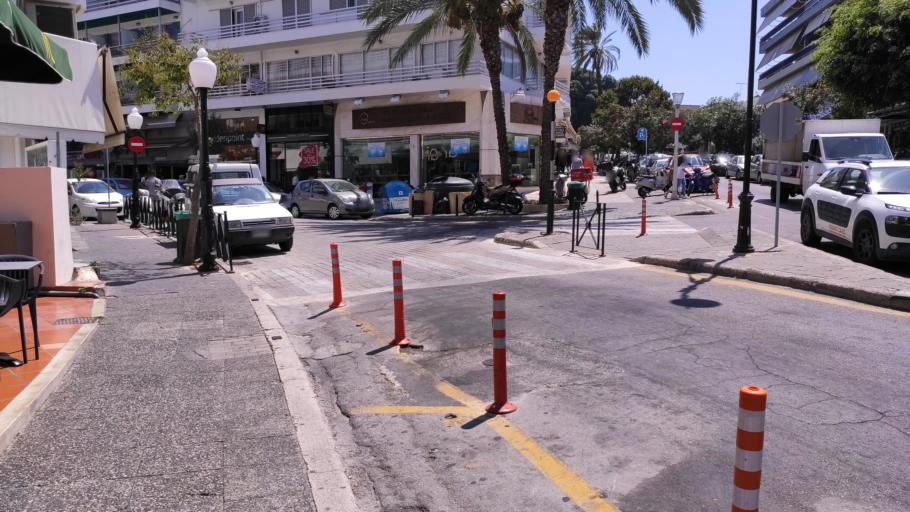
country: GR
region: South Aegean
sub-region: Nomos Dodekanisou
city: Rodos
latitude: 36.4493
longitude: 28.2217
